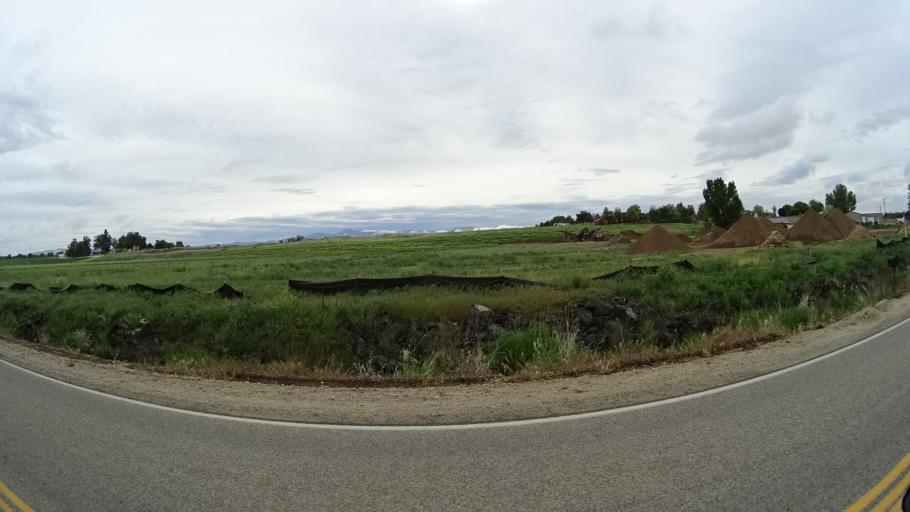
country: US
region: Idaho
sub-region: Ada County
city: Star
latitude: 43.7115
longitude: -116.4683
